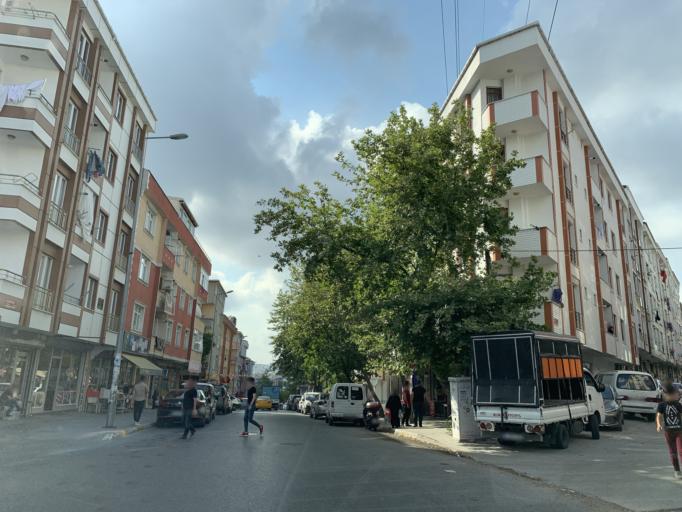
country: TR
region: Istanbul
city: Esenyurt
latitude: 41.0262
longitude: 28.6732
